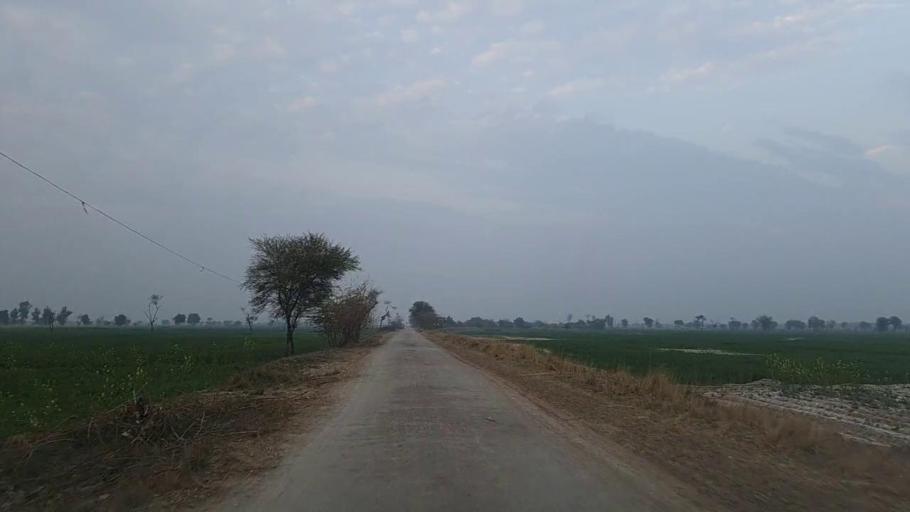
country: PK
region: Sindh
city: Jam Sahib
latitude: 26.3024
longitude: 68.5936
